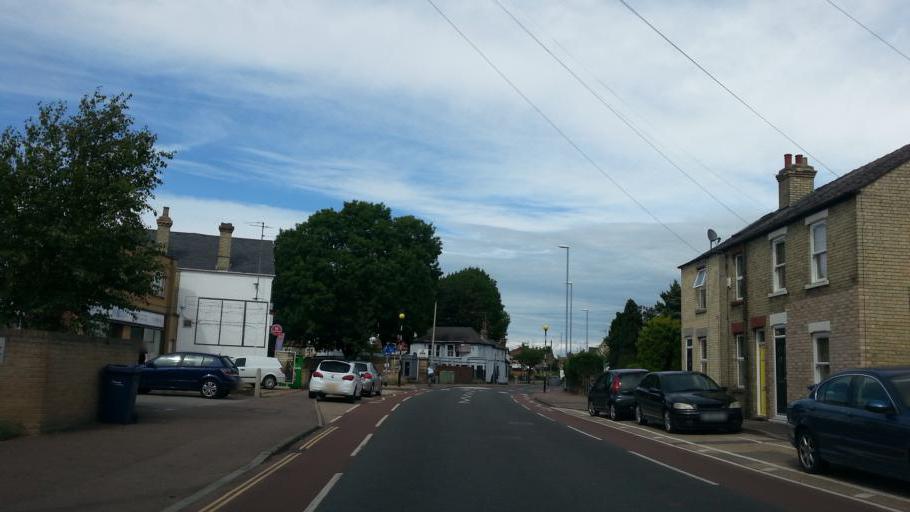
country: GB
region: England
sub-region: Cambridgeshire
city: Fulbourn
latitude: 52.1847
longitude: 0.1725
